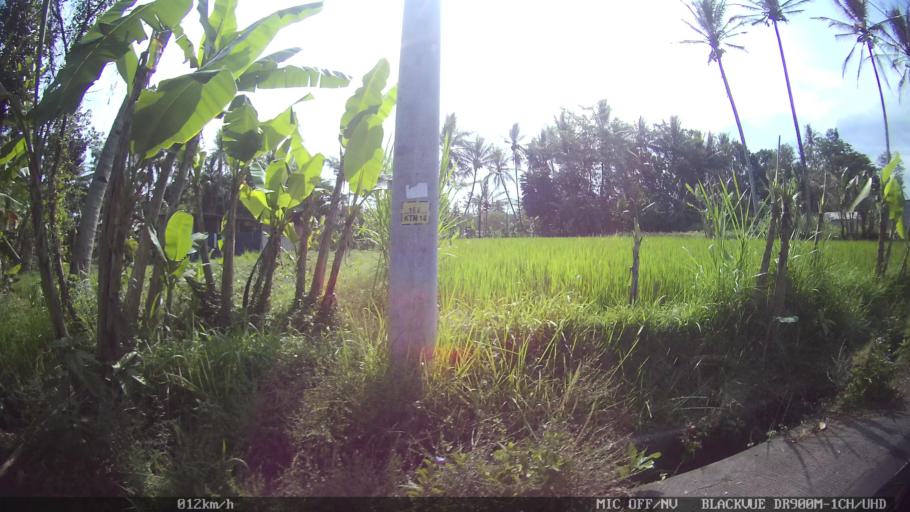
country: ID
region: Daerah Istimewa Yogyakarta
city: Depok
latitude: -7.7273
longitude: 110.4306
